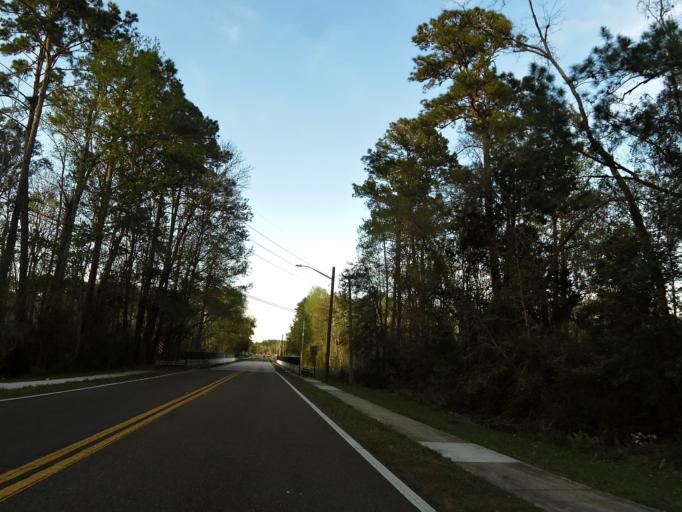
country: US
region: Florida
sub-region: Duval County
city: Jacksonville
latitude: 30.4456
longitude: -81.6713
